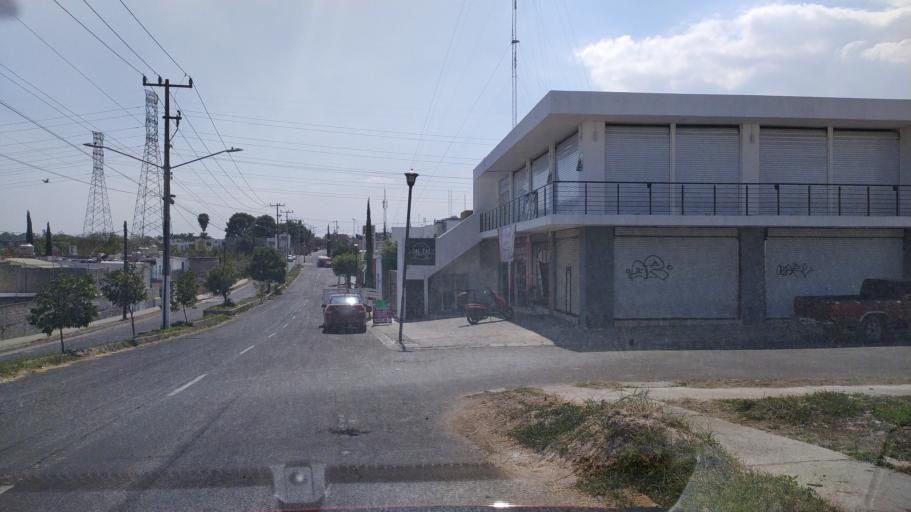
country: MX
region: Jalisco
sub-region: Zapopan
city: Campo Real
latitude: 20.7727
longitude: -103.4342
